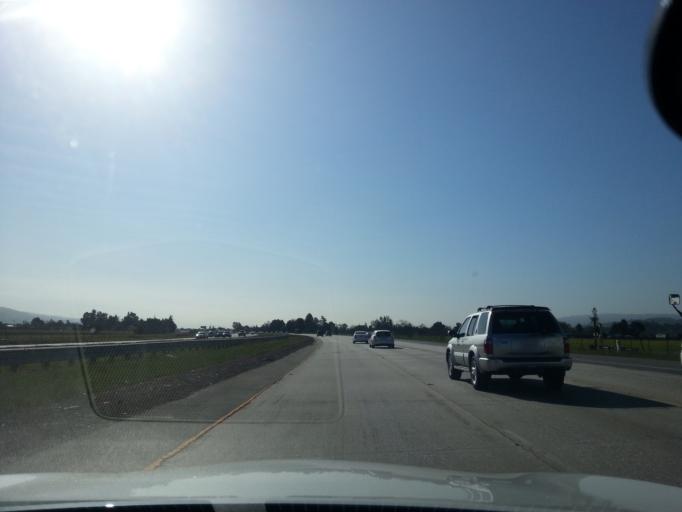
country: US
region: California
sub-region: Santa Clara County
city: Morgan Hill
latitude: 37.1157
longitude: -121.6243
